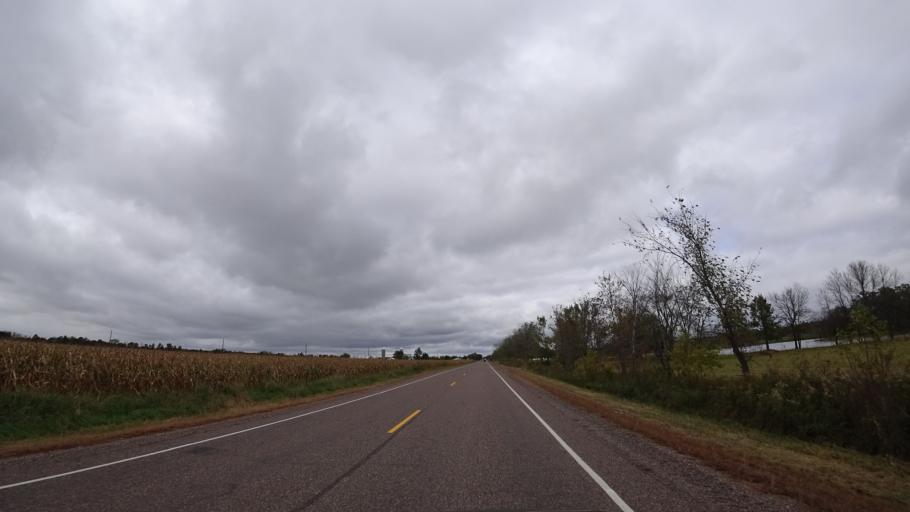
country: US
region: Wisconsin
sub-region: Chippewa County
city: Lake Wissota
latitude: 45.0036
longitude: -91.2867
